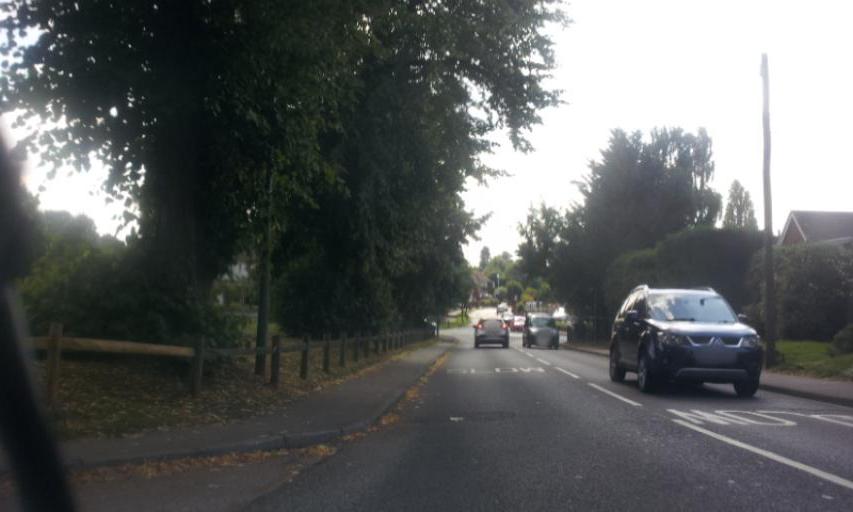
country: GB
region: England
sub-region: Kent
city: Boxley
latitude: 51.2893
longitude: 0.5368
